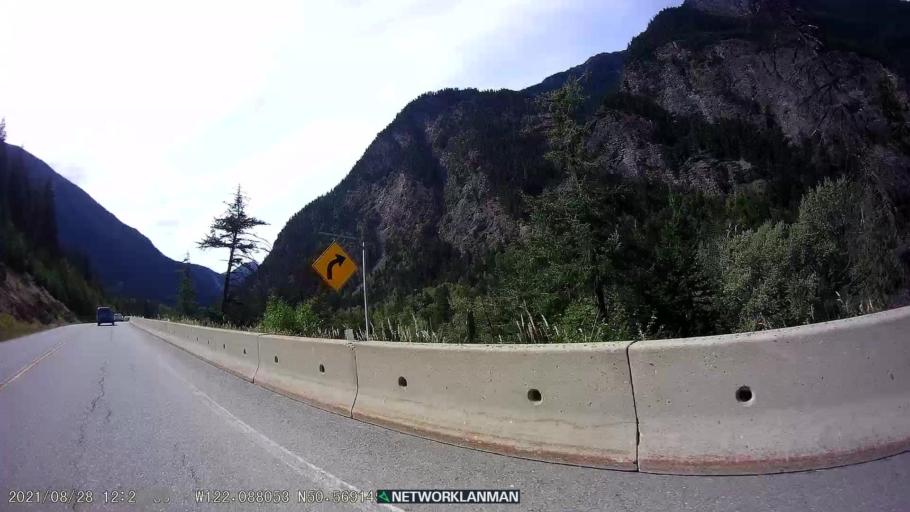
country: CA
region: British Columbia
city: Lillooet
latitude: 50.5668
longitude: -122.0871
